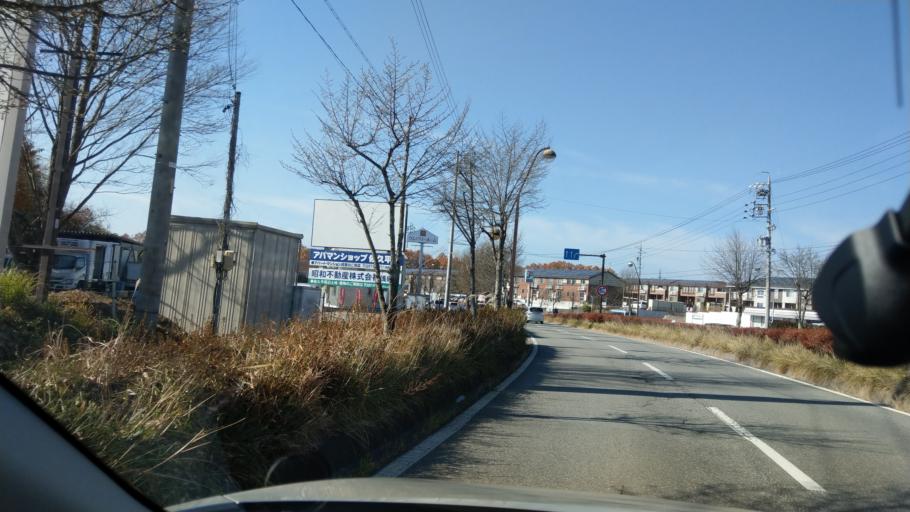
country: JP
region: Nagano
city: Komoro
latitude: 36.2890
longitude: 138.4760
